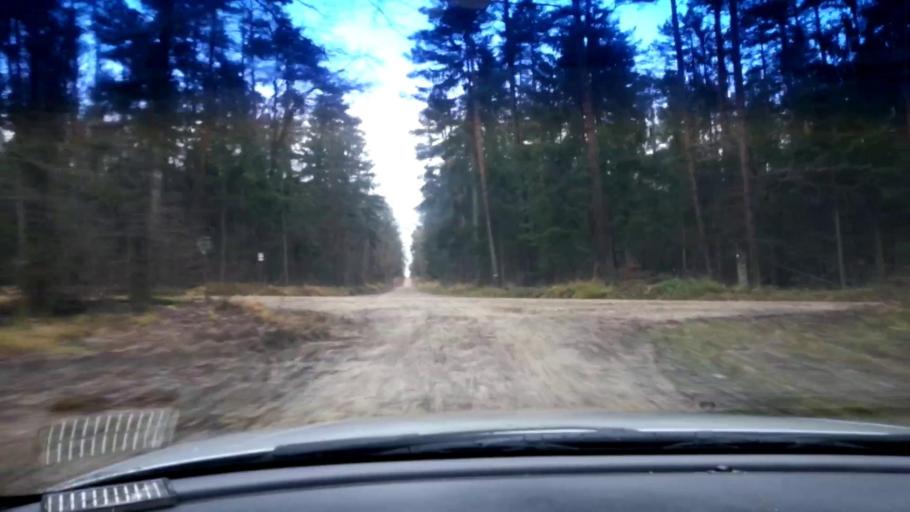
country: DE
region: Bavaria
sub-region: Upper Franconia
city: Breitengussbach
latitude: 49.9558
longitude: 10.9009
